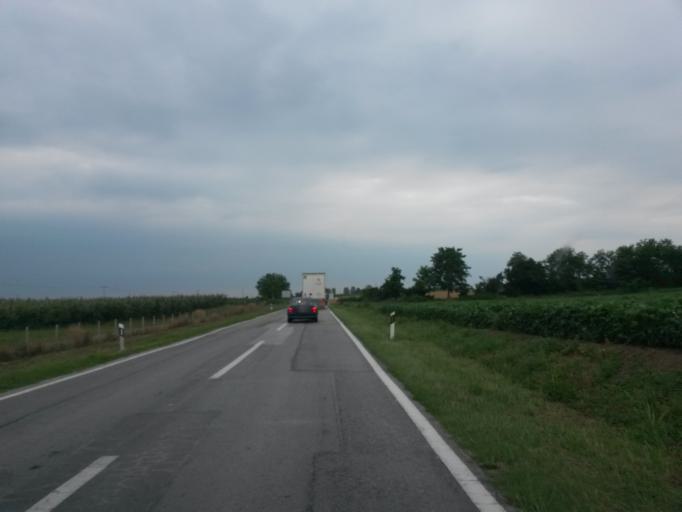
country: HR
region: Vukovarsko-Srijemska
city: Lovas
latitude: 45.2545
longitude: 19.1941
